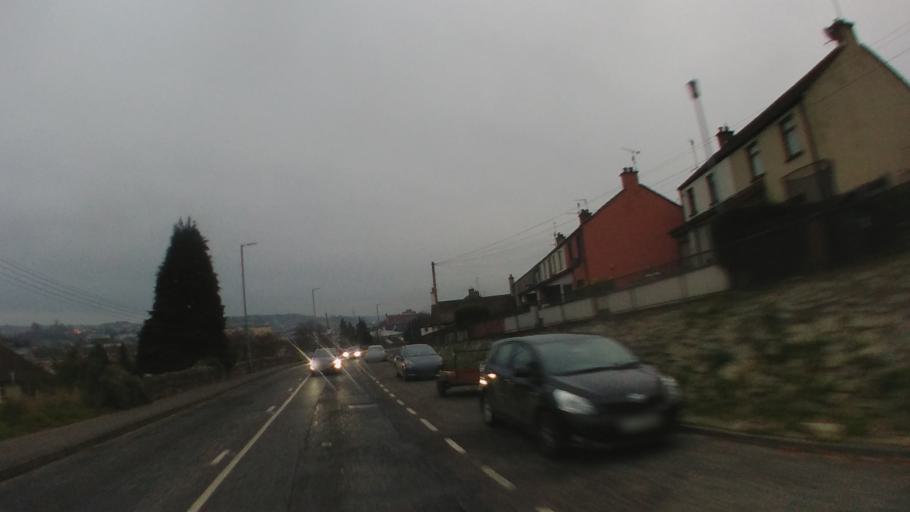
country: GB
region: Northern Ireland
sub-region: Newry and Mourne District
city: Newry
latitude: 54.1798
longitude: -6.3485
